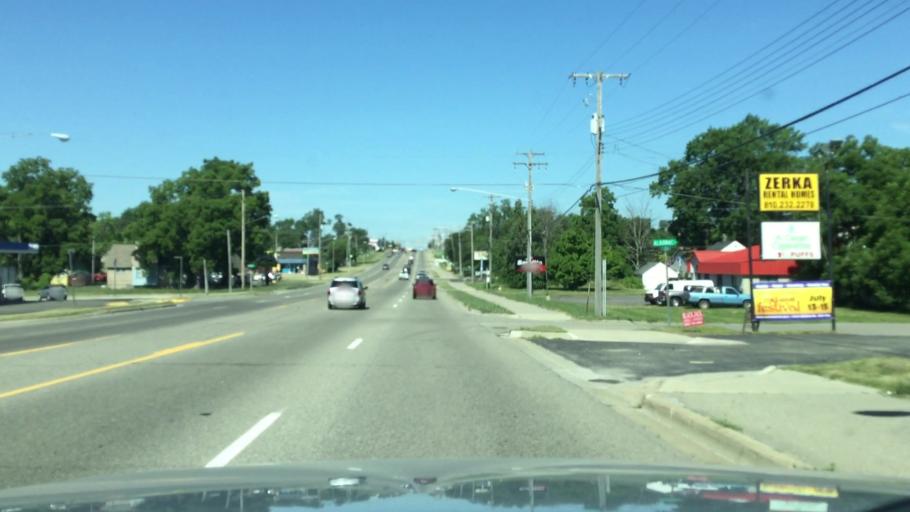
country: US
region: Michigan
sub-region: Genesee County
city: Flint
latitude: 43.0021
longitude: -83.7560
